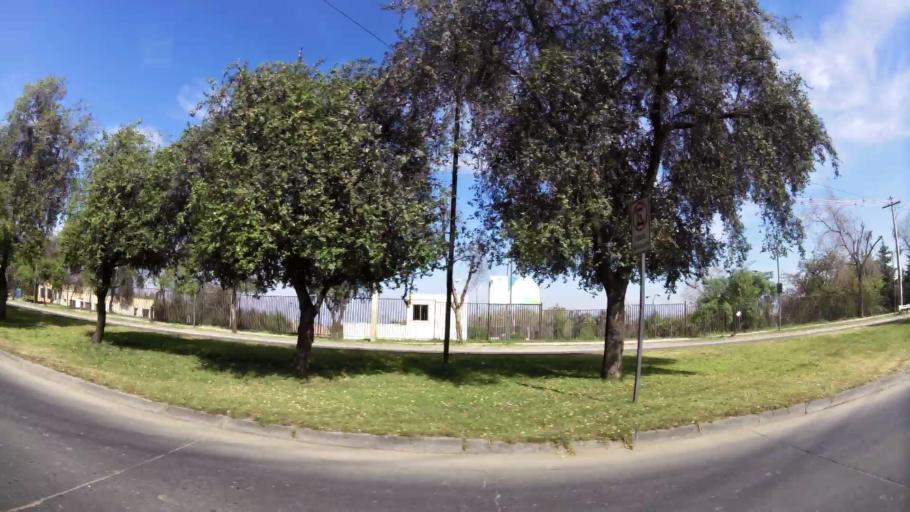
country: CL
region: Santiago Metropolitan
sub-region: Provincia de Santiago
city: Villa Presidente Frei, Nunoa, Santiago, Chile
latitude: -33.4316
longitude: -70.5389
